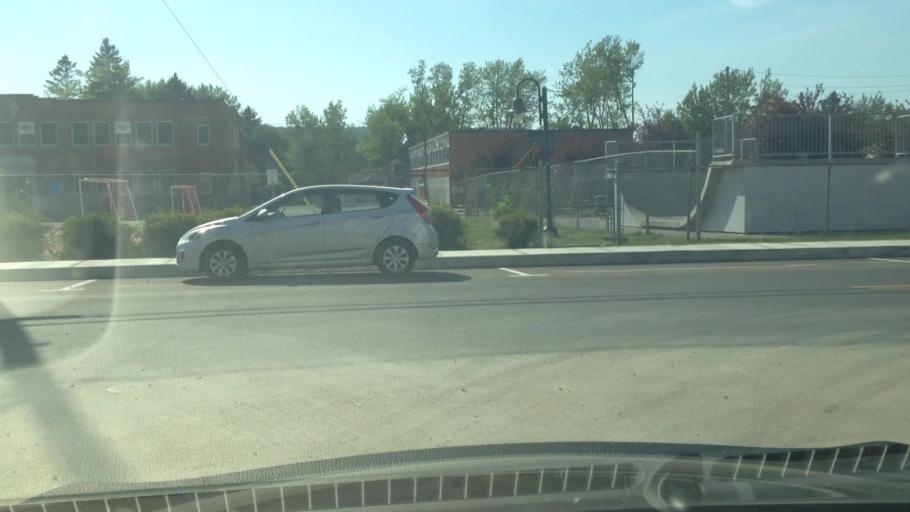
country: CA
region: Quebec
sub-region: Laurentides
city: Mont-Tremblant
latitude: 46.1215
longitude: -74.5920
